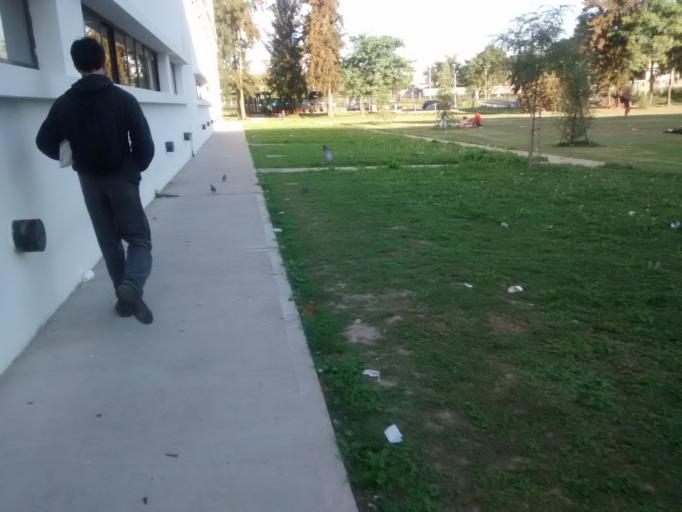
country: AR
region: Buenos Aires
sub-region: Partido de La Plata
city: La Plata
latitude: -34.9006
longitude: -57.9323
